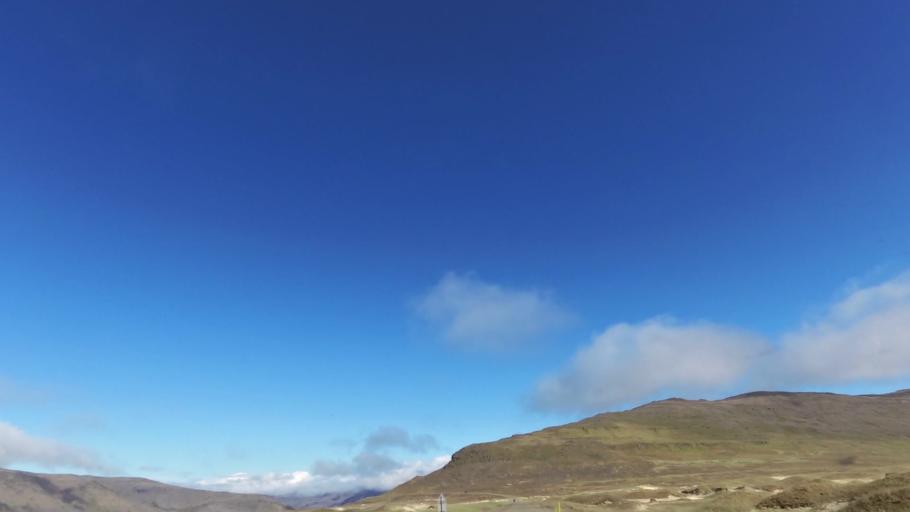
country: IS
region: West
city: Olafsvik
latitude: 65.5567
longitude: -23.9844
